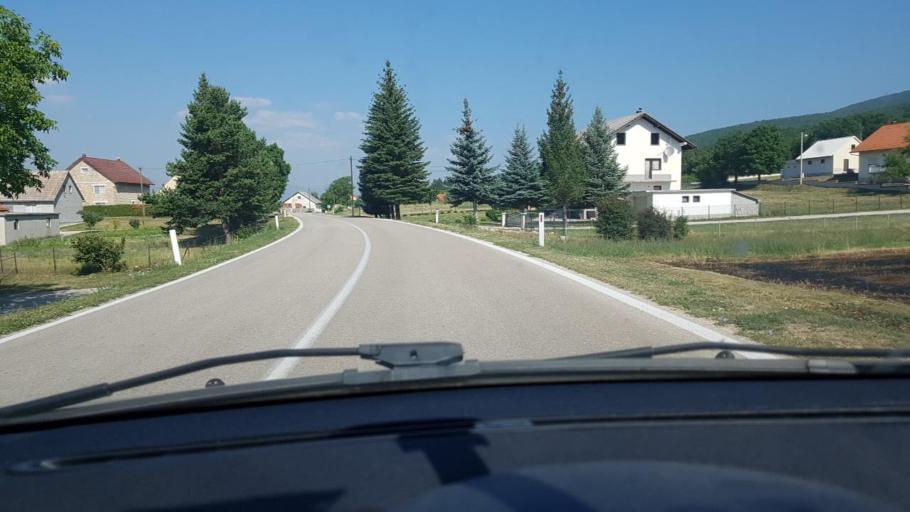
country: BA
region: Federation of Bosnia and Herzegovina
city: Orguz
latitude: 43.8710
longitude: 16.8754
